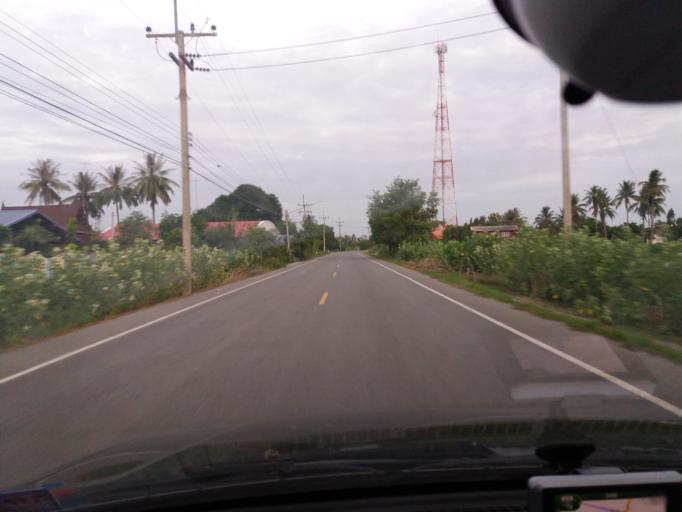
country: TH
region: Suphan Buri
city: Don Chedi
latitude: 14.7055
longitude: 100.0269
